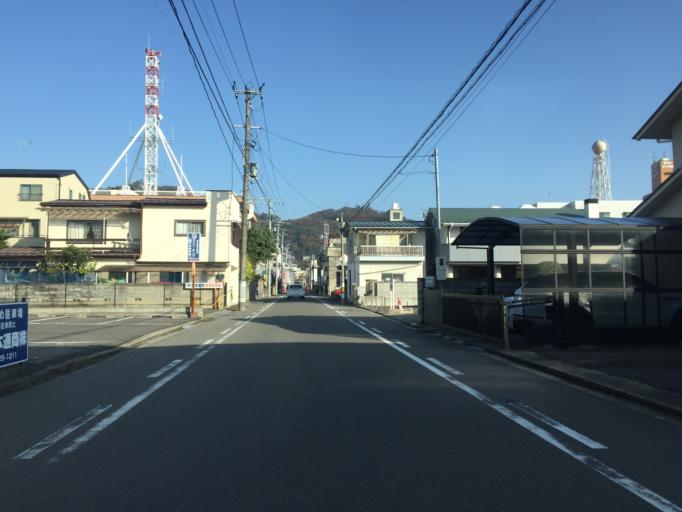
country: JP
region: Fukushima
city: Fukushima-shi
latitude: 37.7591
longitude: 140.4651
